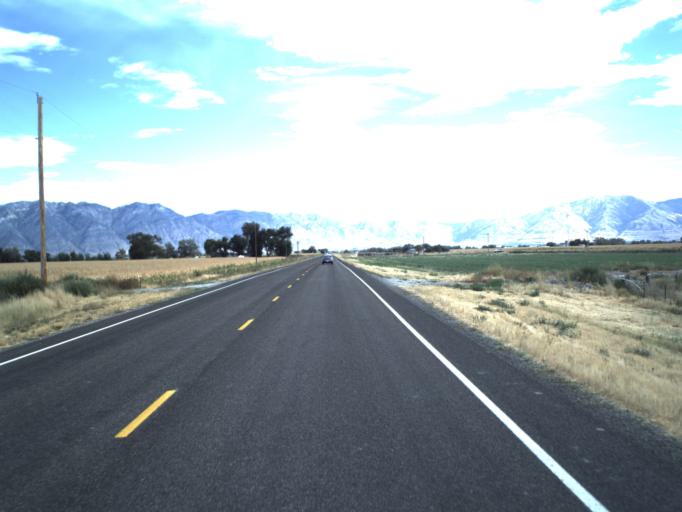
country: US
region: Utah
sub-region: Box Elder County
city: Elwood
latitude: 41.5705
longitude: -112.2037
